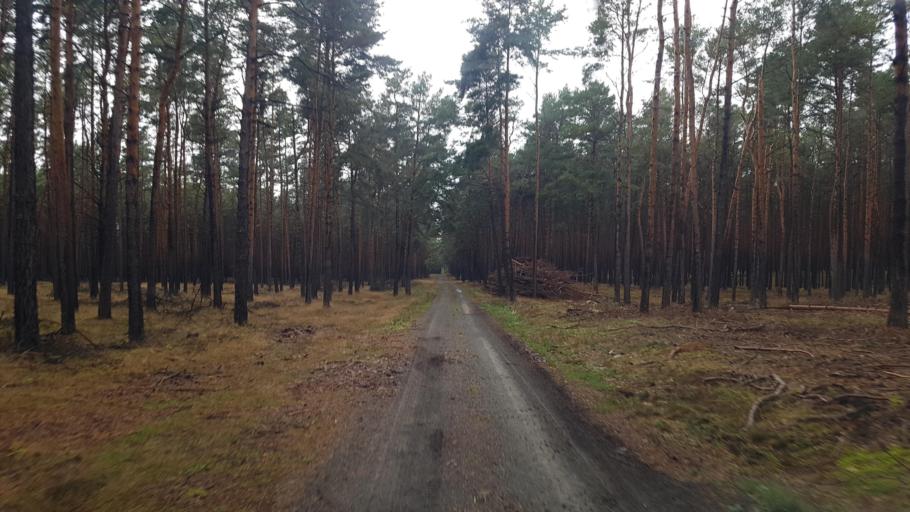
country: DE
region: Brandenburg
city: Schlieben
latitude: 51.7391
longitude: 13.3448
